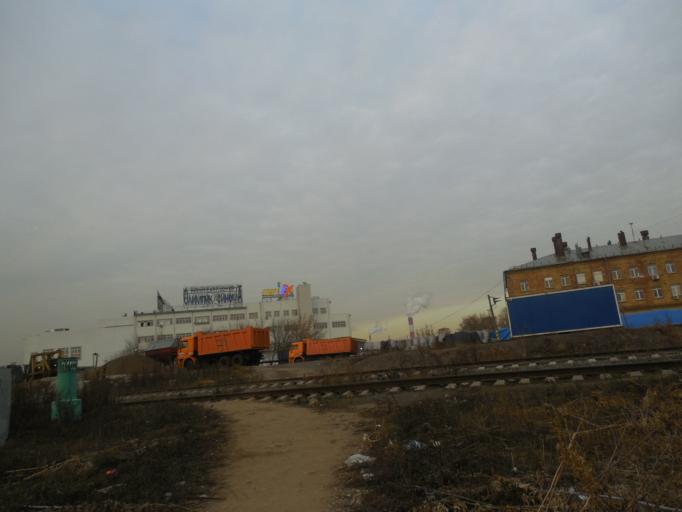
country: RU
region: Moscow
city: Lefortovo
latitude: 55.7358
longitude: 37.7161
